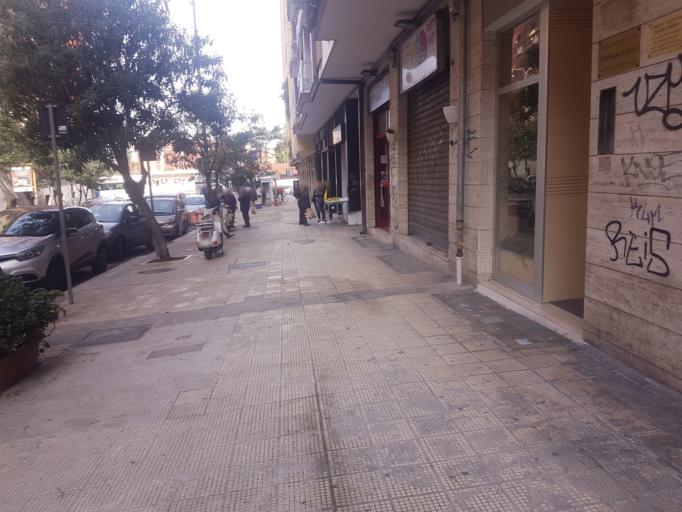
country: IT
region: Apulia
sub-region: Provincia di Bari
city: Bari
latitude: 41.1157
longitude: 16.8625
